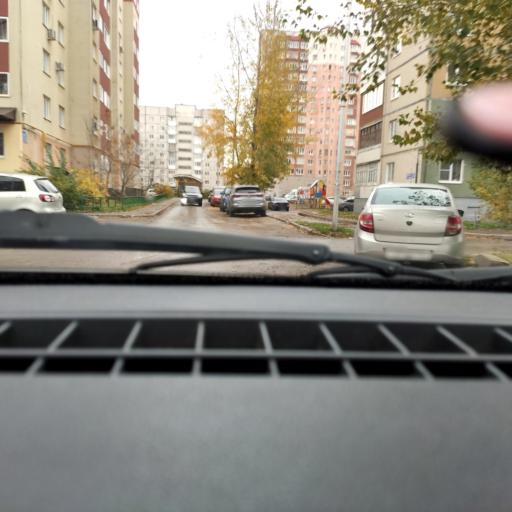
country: RU
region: Bashkortostan
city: Ufa
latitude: 54.7823
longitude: 56.1101
